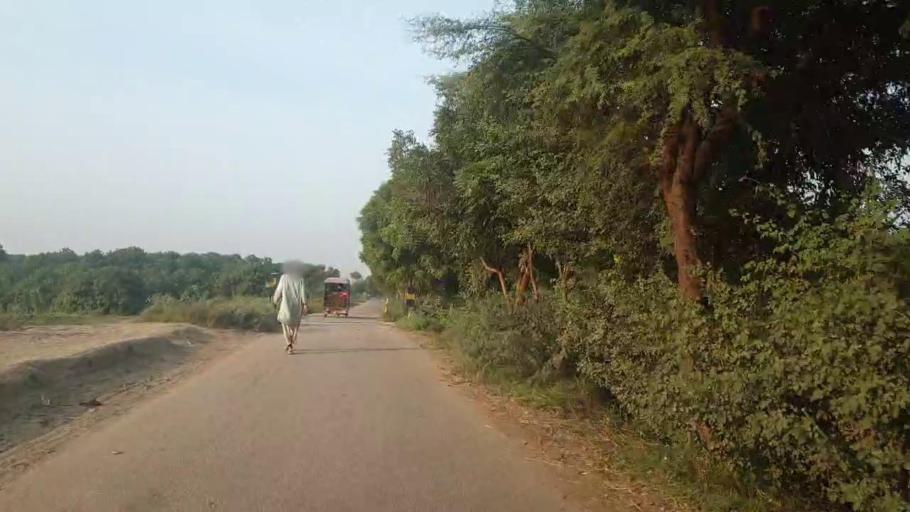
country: PK
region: Sindh
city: Tando Jam
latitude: 25.4458
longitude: 68.5849
